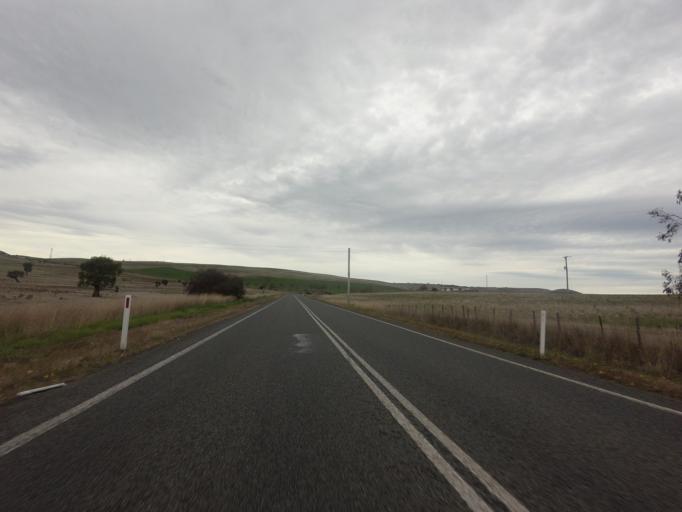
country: AU
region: Tasmania
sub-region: Derwent Valley
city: New Norfolk
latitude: -42.5529
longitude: 146.7991
